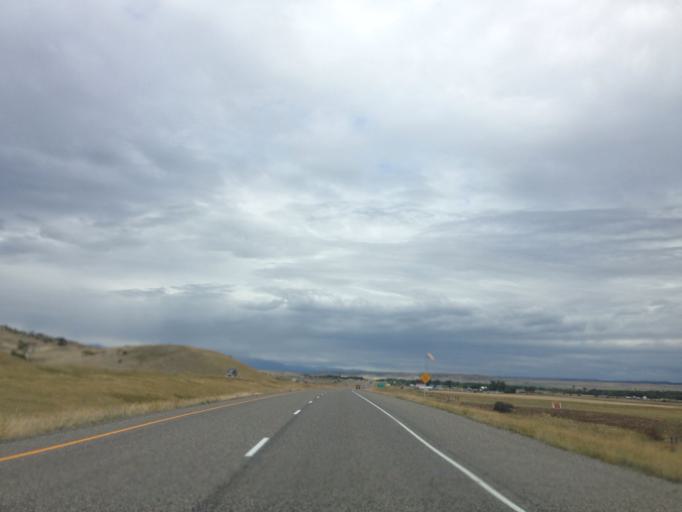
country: US
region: Montana
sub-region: Sweet Grass County
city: Big Timber
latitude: 45.7509
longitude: -109.7770
